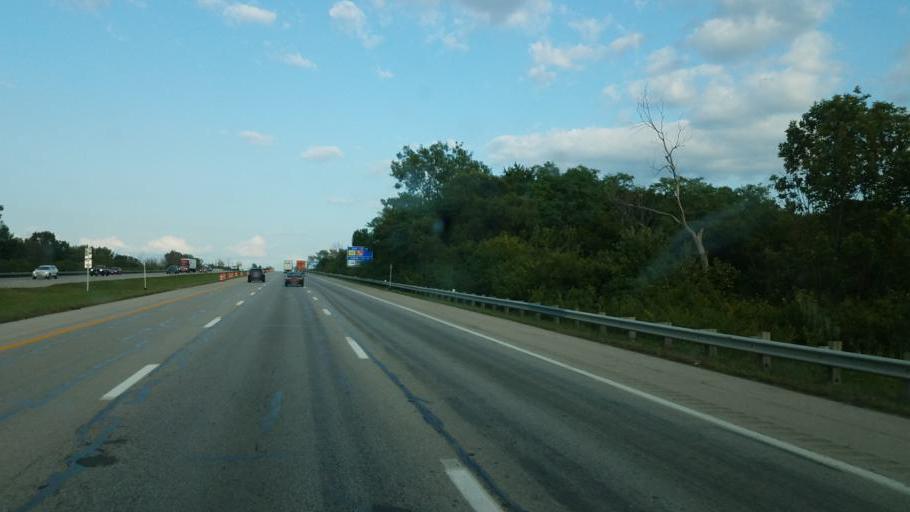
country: US
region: Ohio
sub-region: Franklin County
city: Obetz
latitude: 39.8724
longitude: -82.9647
